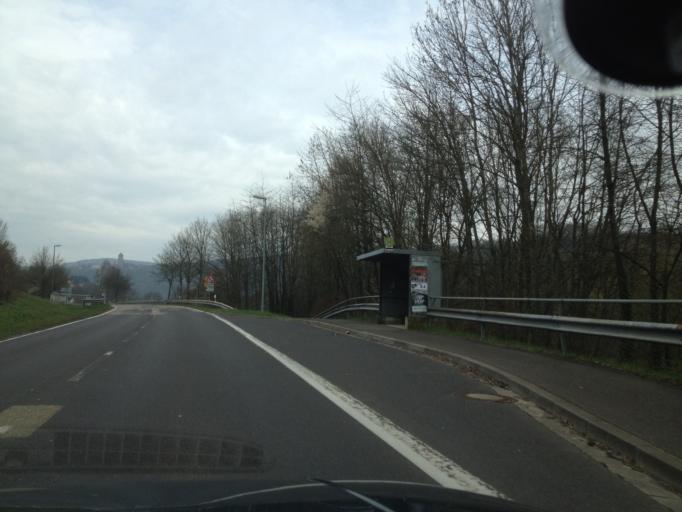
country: DE
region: Rheinland-Pfalz
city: Ruthweiler
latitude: 49.5468
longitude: 7.3787
